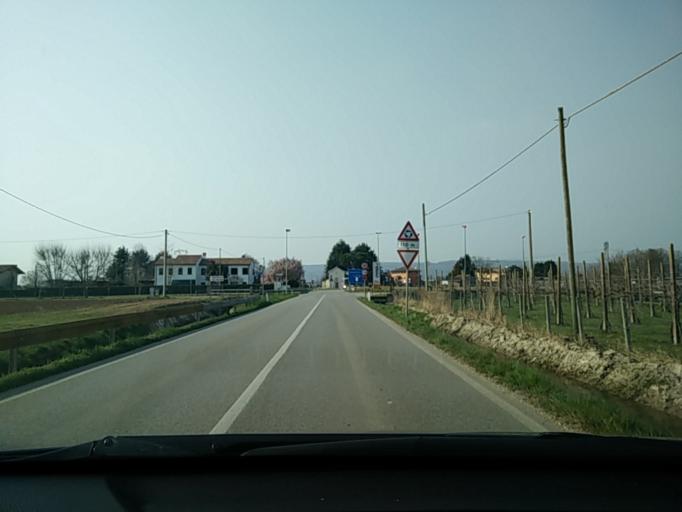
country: IT
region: Veneto
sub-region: Provincia di Treviso
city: Camalo
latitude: 45.7617
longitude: 12.1583
